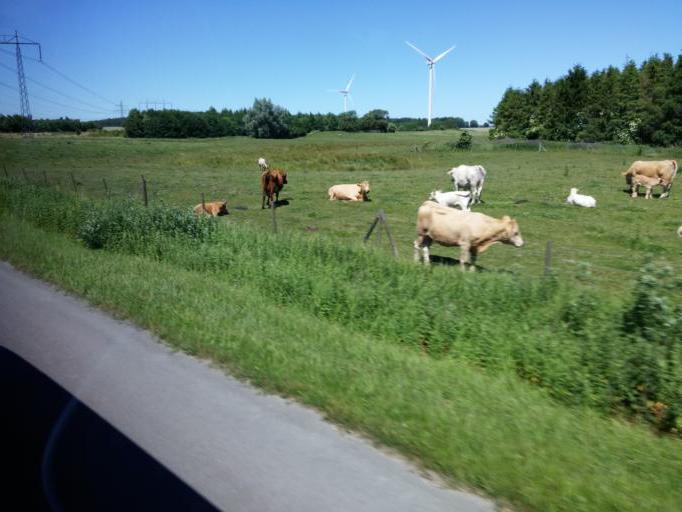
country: SE
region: Skane
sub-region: Svedala Kommun
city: Svedala
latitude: 55.5315
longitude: 13.1887
